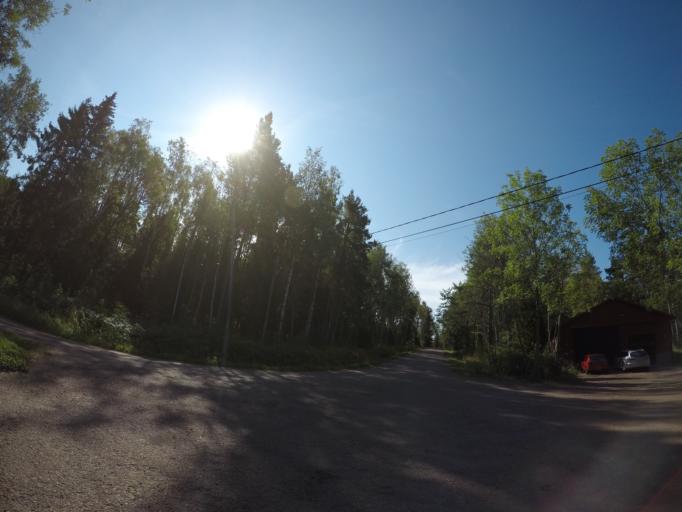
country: AX
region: Alands landsbygd
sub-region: Finstroem
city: Finstroem
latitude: 60.2815
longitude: 19.9167
